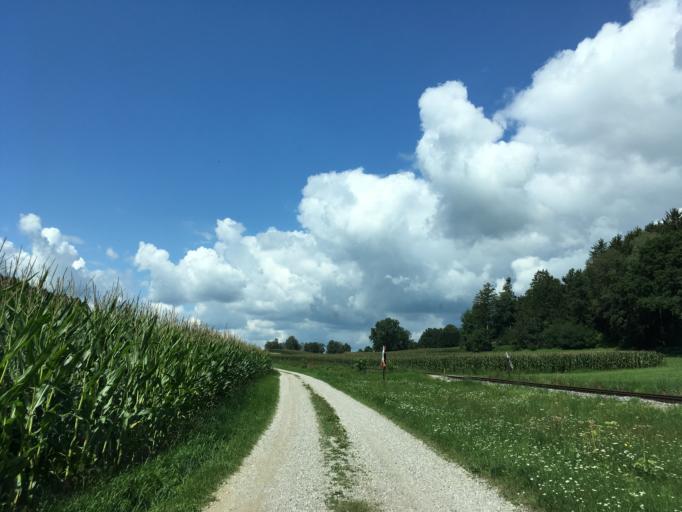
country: DE
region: Bavaria
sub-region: Upper Bavaria
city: Pittenhart
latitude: 47.9863
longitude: 12.3491
